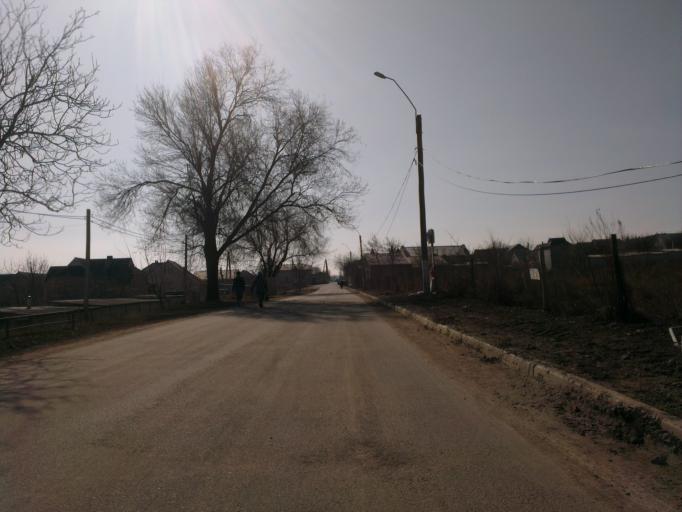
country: MD
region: Chisinau
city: Ciorescu
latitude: 47.1251
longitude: 28.8846
